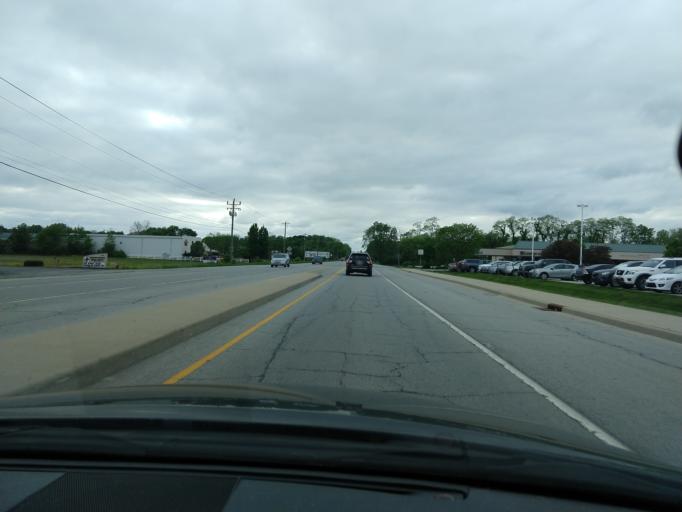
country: US
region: Indiana
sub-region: Hamilton County
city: Westfield
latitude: 40.0429
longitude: -86.1111
